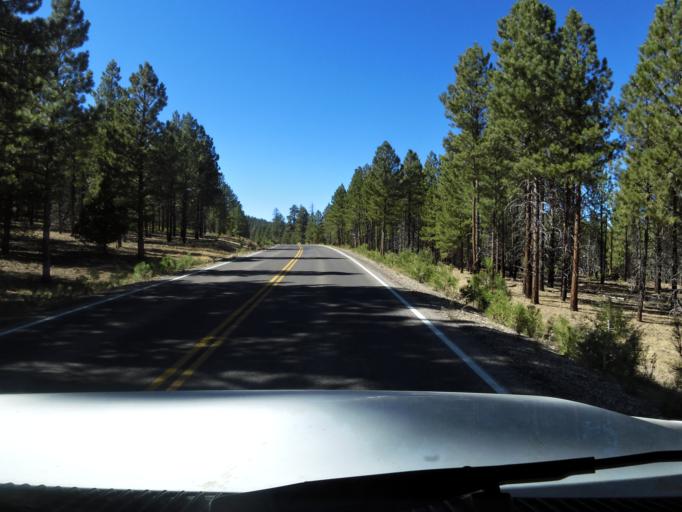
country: US
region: Utah
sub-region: Garfield County
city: Panguitch
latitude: 37.6070
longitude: -112.1959
